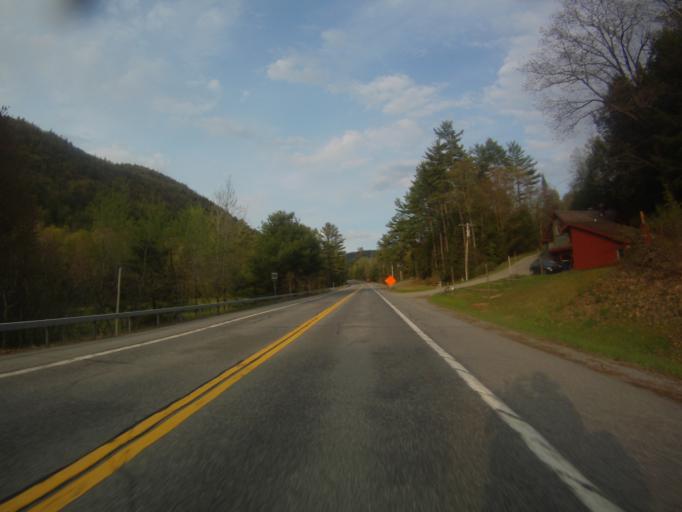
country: US
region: New York
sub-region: Essex County
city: Ticonderoga
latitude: 43.7418
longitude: -73.6519
